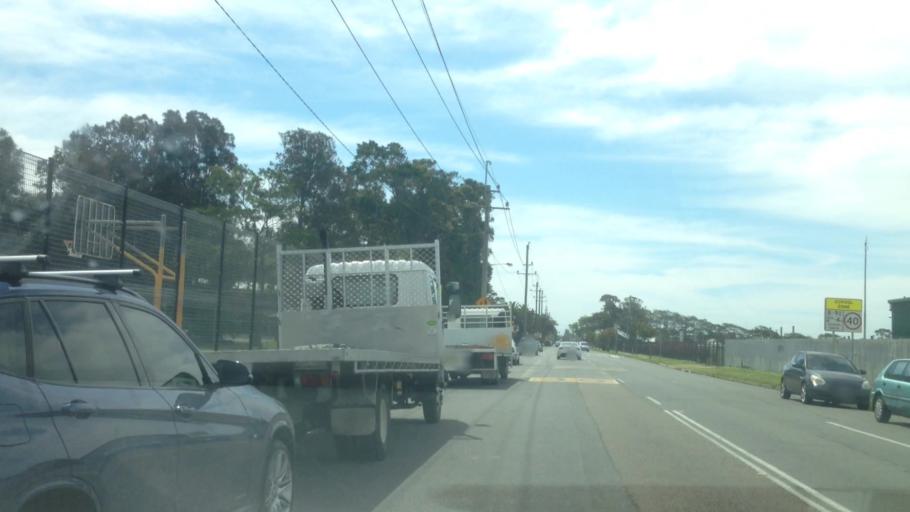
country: AU
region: New South Wales
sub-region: Newcastle
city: Broadmeadow
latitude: -32.9308
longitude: 151.7361
